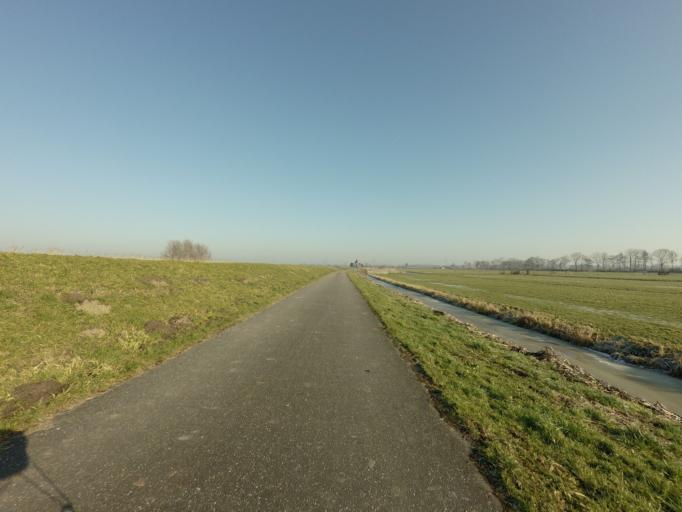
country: NL
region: Utrecht
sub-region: Stichtse Vecht
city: Breukelen
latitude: 52.1623
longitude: 4.9658
